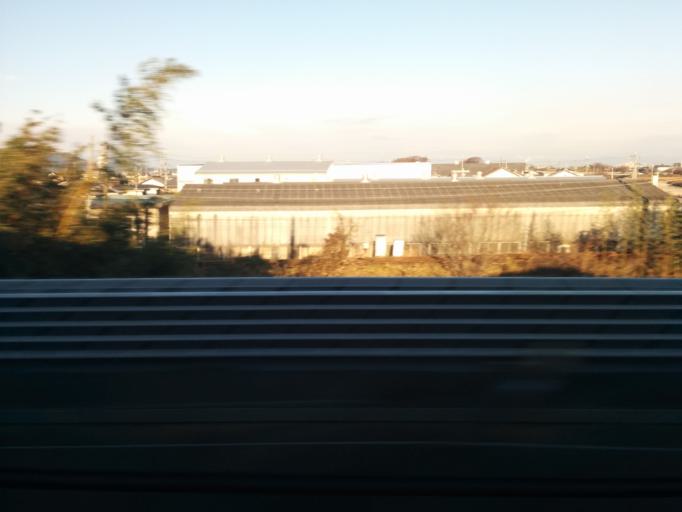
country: JP
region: Shiga Prefecture
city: Hikone
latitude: 35.2259
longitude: 136.2575
